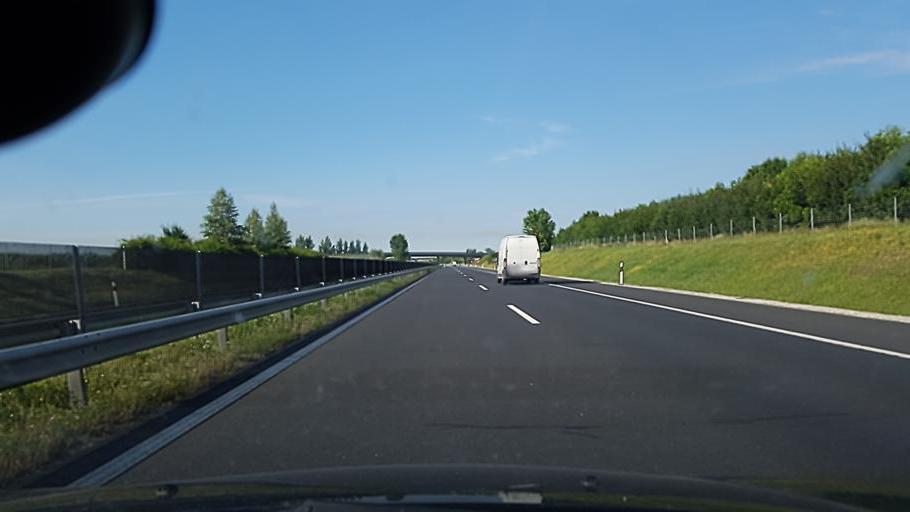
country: HU
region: Fejer
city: Racalmas
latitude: 47.0159
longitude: 18.8964
